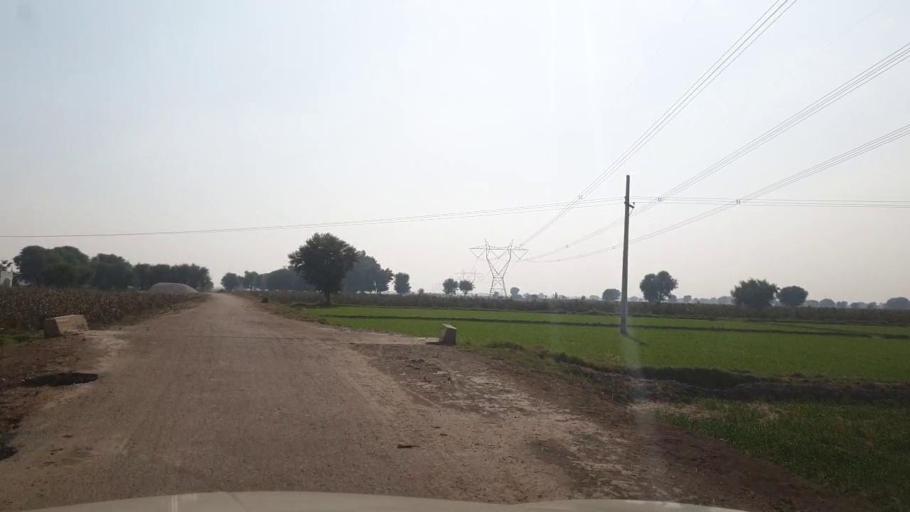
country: PK
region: Sindh
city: Bhan
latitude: 26.5426
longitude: 67.7490
